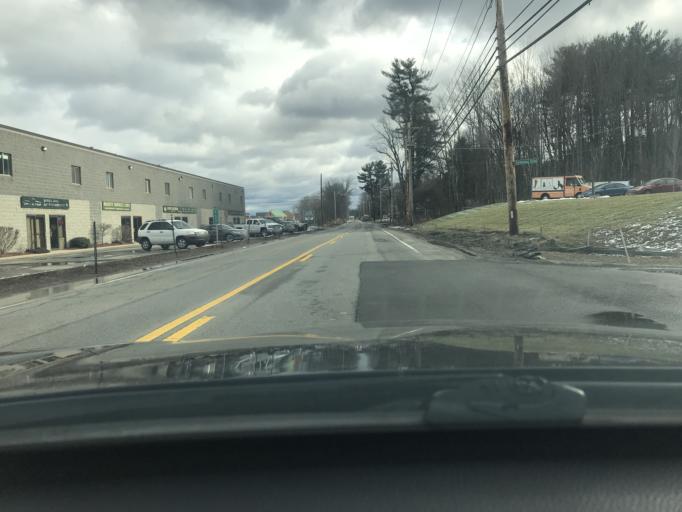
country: US
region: Massachusetts
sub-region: Middlesex County
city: Tyngsboro
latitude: 42.6687
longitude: -71.4148
